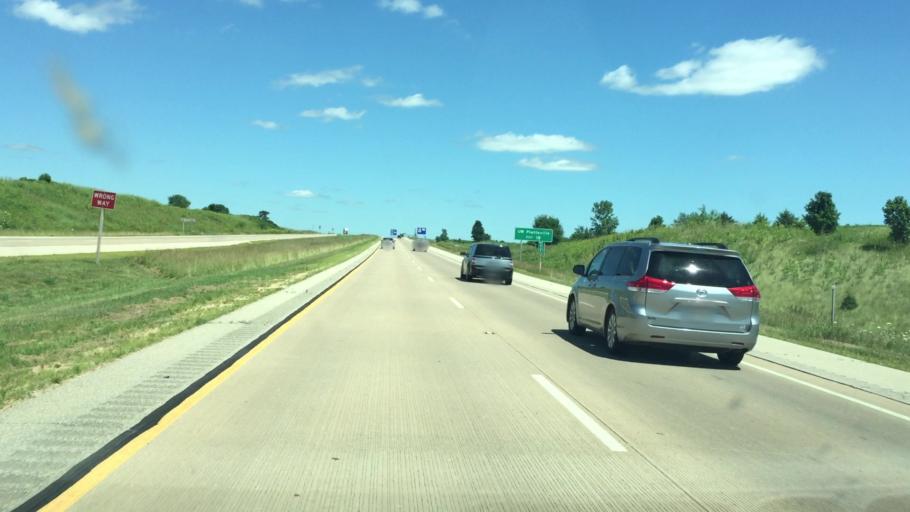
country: US
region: Wisconsin
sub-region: Grant County
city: Platteville
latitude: 42.7108
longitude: -90.5040
